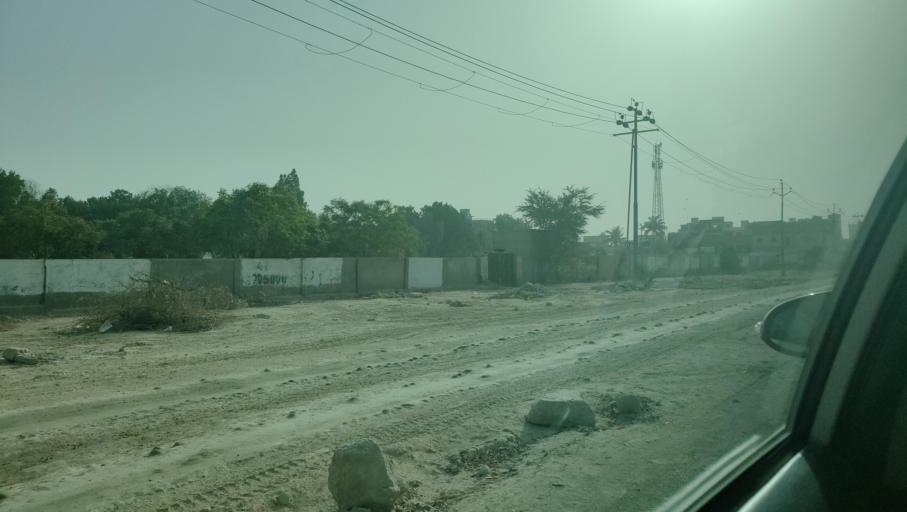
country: PK
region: Sindh
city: Malir Cantonment
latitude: 24.9373
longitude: 67.1657
